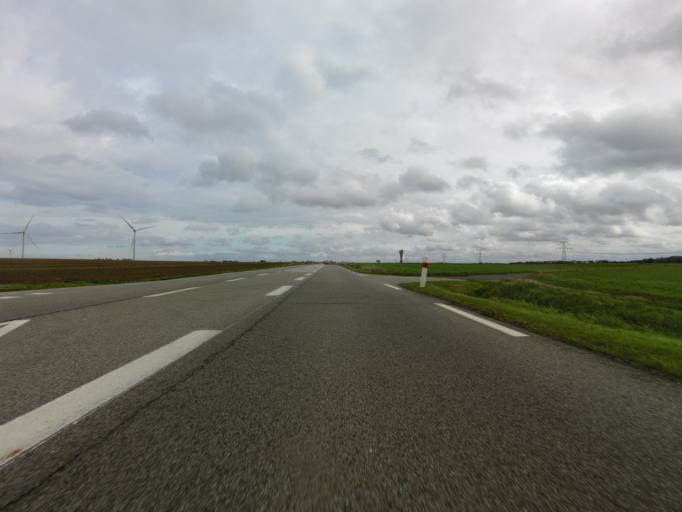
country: FR
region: Haute-Normandie
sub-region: Departement de la Seine-Maritime
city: Le Treport
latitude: 50.0187
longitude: 1.3610
